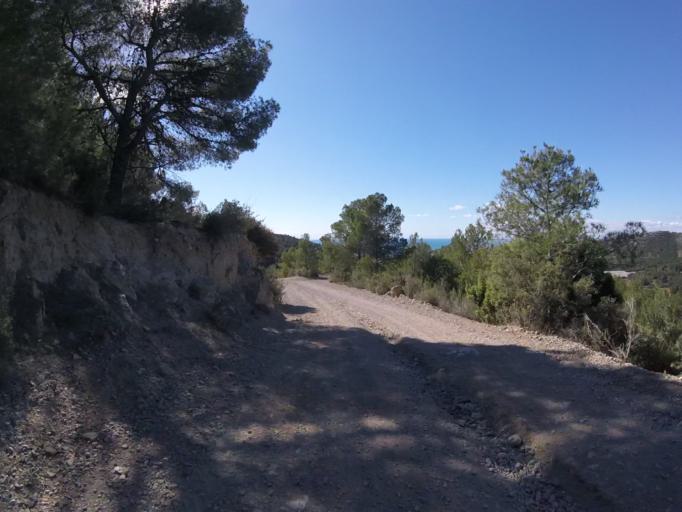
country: ES
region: Valencia
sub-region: Provincia de Castello
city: Benicassim
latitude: 40.0746
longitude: 0.0768
